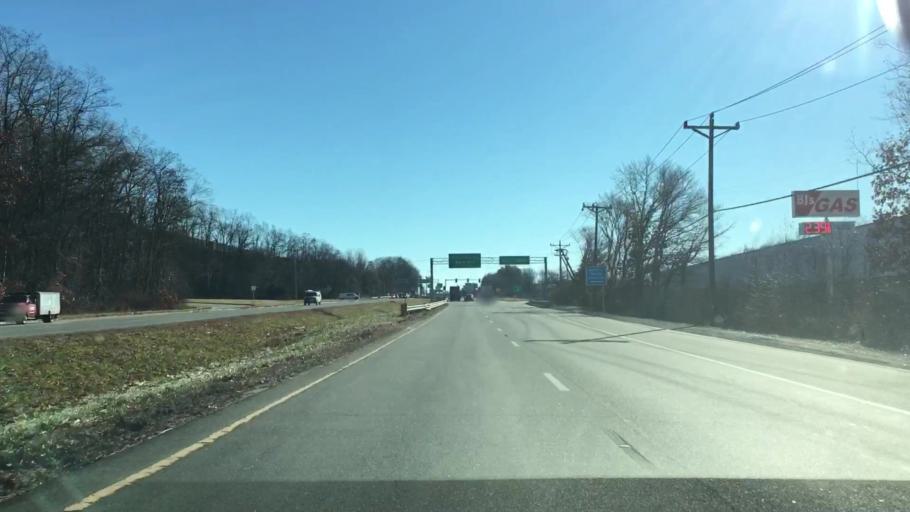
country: US
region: Massachusetts
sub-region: Essex County
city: Haverhill
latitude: 42.7582
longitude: -71.1166
